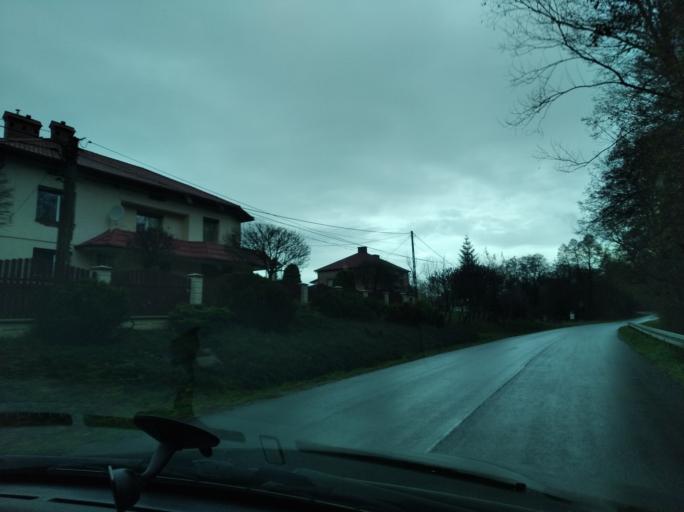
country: PL
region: Subcarpathian Voivodeship
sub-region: Powiat rzeszowski
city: Lecka
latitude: 49.9040
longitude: 22.0192
